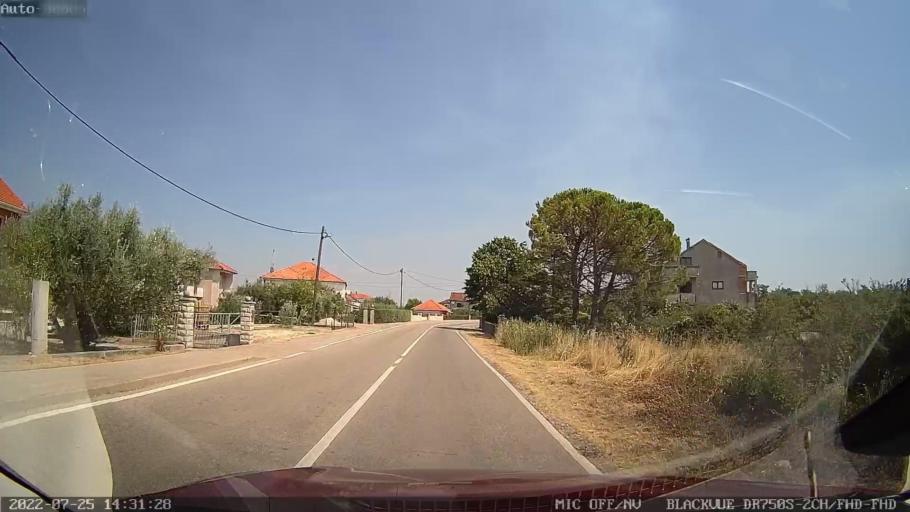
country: HR
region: Zadarska
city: Galovac
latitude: 44.1102
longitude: 15.3723
